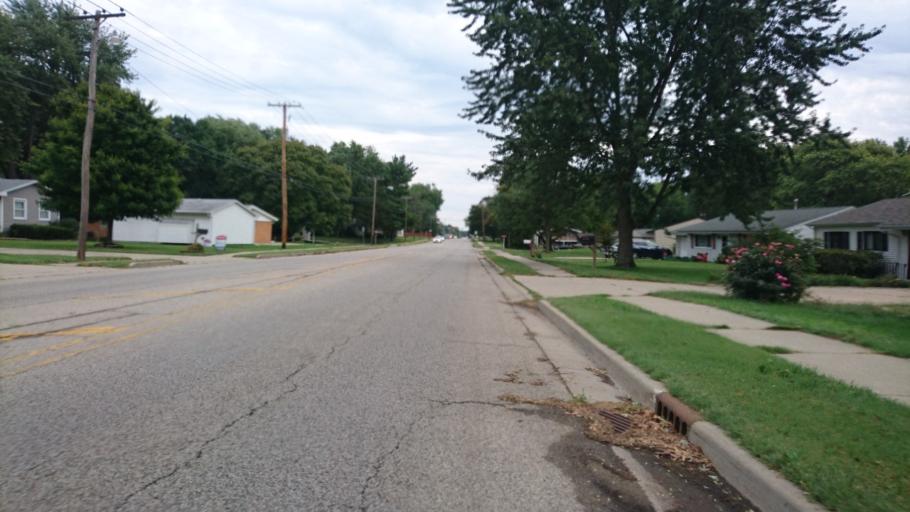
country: US
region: Illinois
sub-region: Sangamon County
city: Chatham
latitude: 39.6768
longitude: -89.6856
